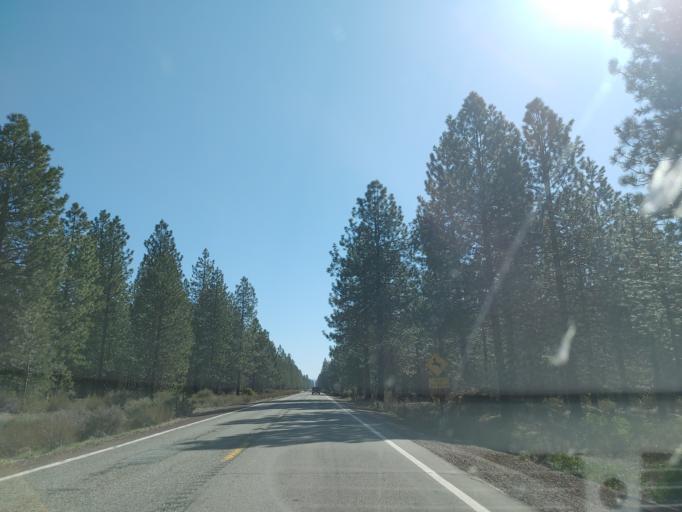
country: US
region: California
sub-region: Siskiyou County
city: McCloud
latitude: 41.2525
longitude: -122.1018
